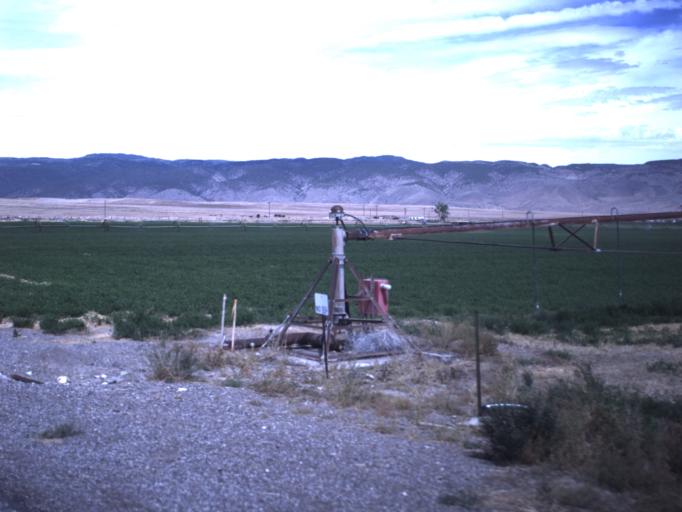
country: US
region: Utah
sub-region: Sevier County
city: Monroe
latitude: 38.6289
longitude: -112.1574
